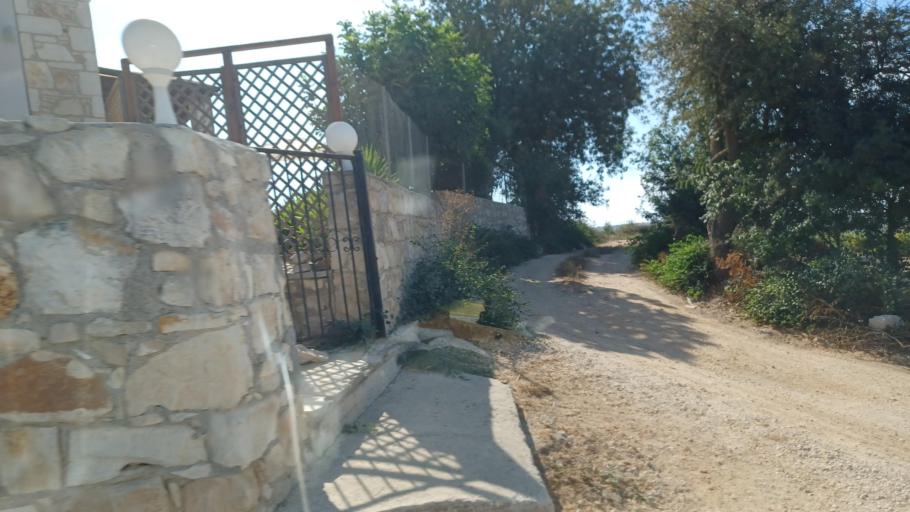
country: CY
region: Pafos
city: Pegeia
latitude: 34.9076
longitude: 32.4241
